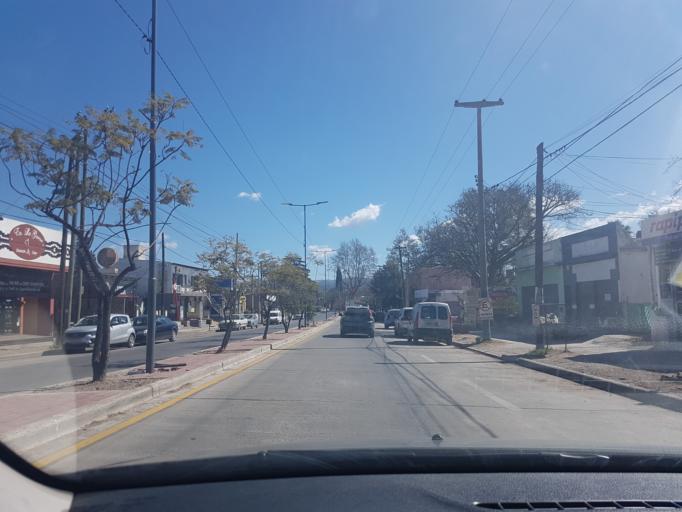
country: AR
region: Cordoba
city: Villa Allende
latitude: -31.2983
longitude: -64.2899
